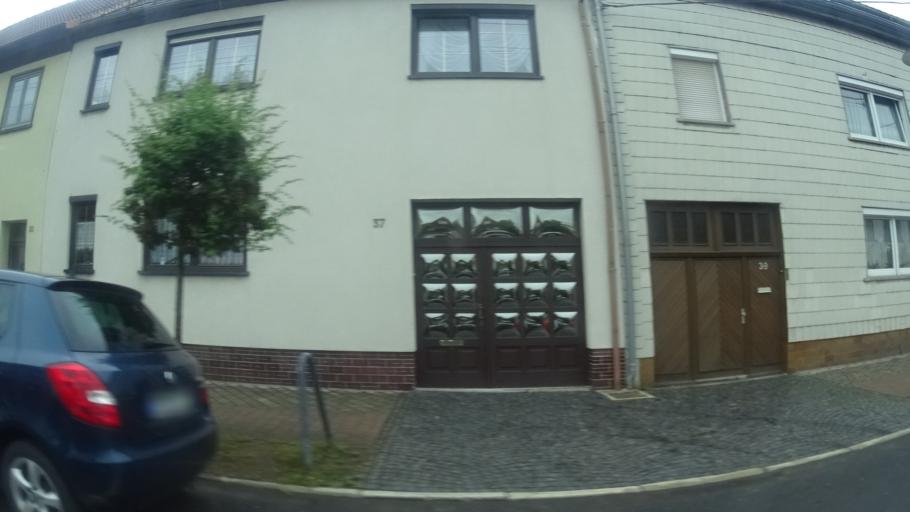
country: DE
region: Thuringia
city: Langewiesen
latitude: 50.6726
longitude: 10.9724
